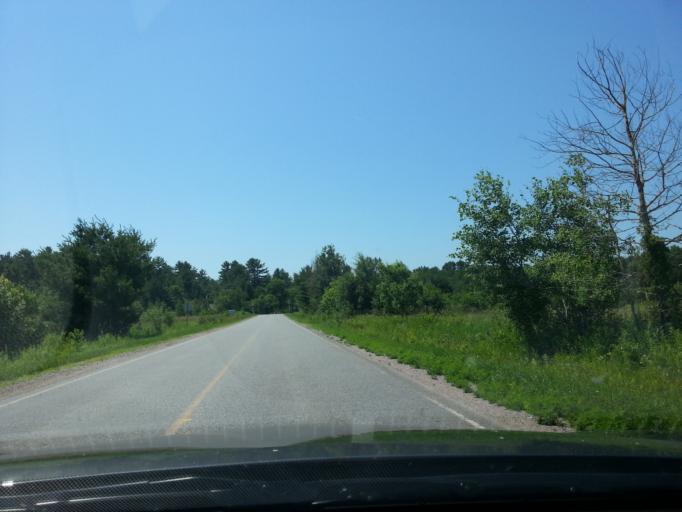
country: CA
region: Ontario
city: Arnprior
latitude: 45.5197
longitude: -76.4052
